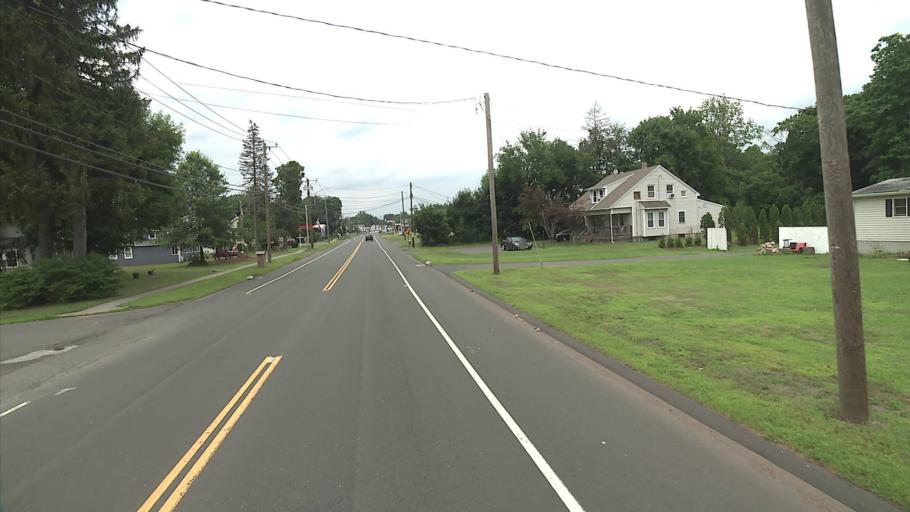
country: US
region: Connecticut
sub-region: Middlesex County
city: Cromwell
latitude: 41.6153
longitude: -72.6530
